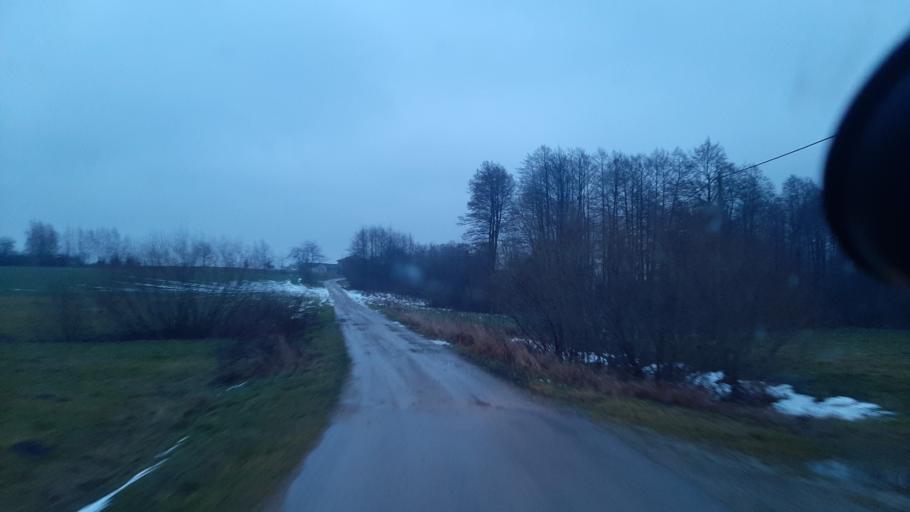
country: PL
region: Lublin Voivodeship
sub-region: Powiat lubelski
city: Jastkow
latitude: 51.3859
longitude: 22.4159
